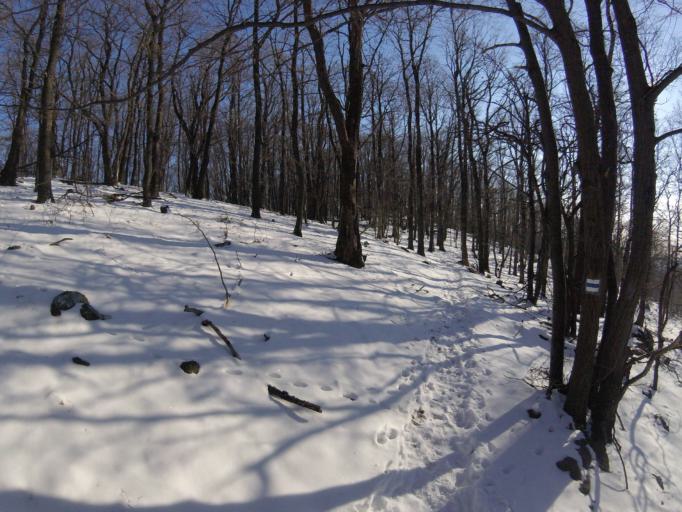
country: HU
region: Heves
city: Parad
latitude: 47.8675
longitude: 20.0465
